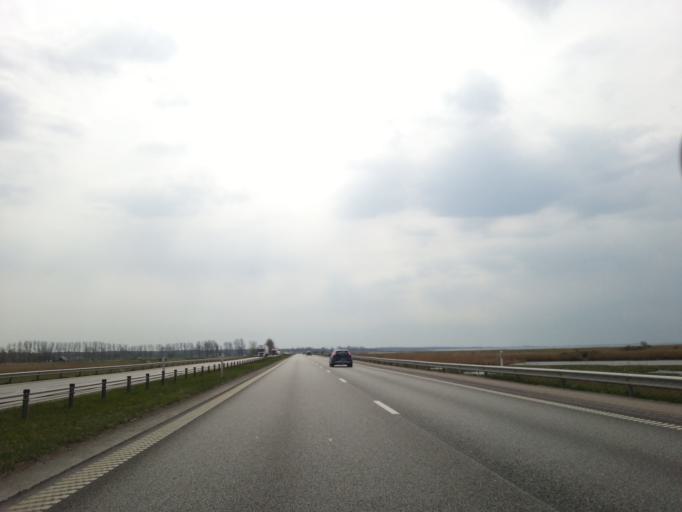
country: SE
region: Skane
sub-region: Landskrona
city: Asmundtorp
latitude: 55.8568
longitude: 12.8897
